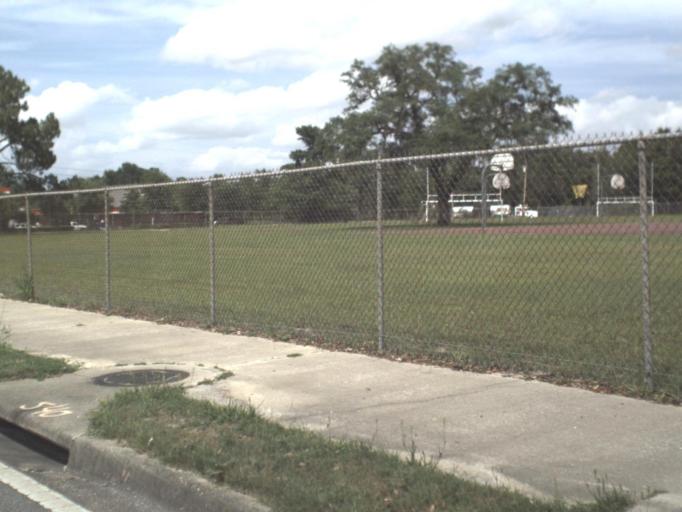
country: US
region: Florida
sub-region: Clay County
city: Middleburg
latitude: 30.0699
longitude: -81.8657
